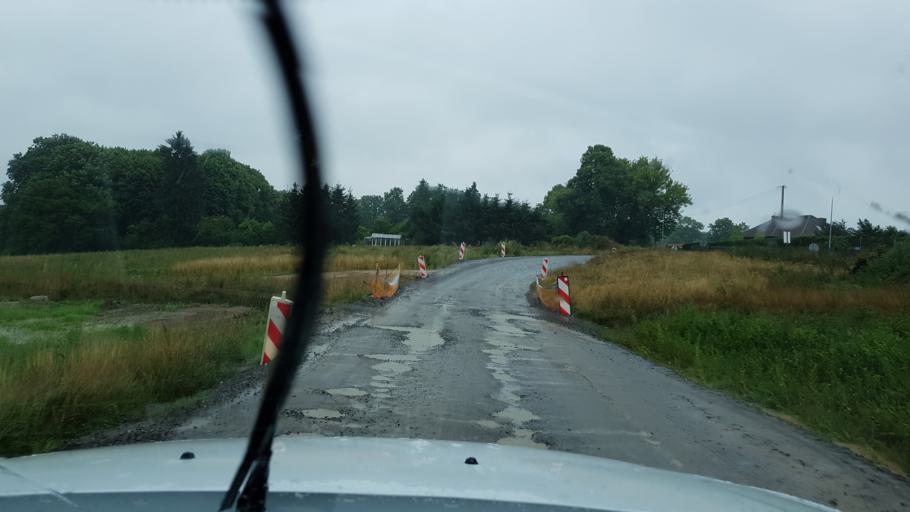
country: PL
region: West Pomeranian Voivodeship
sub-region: Powiat kolobrzeski
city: Grzybowo
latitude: 54.0912
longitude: 15.5202
